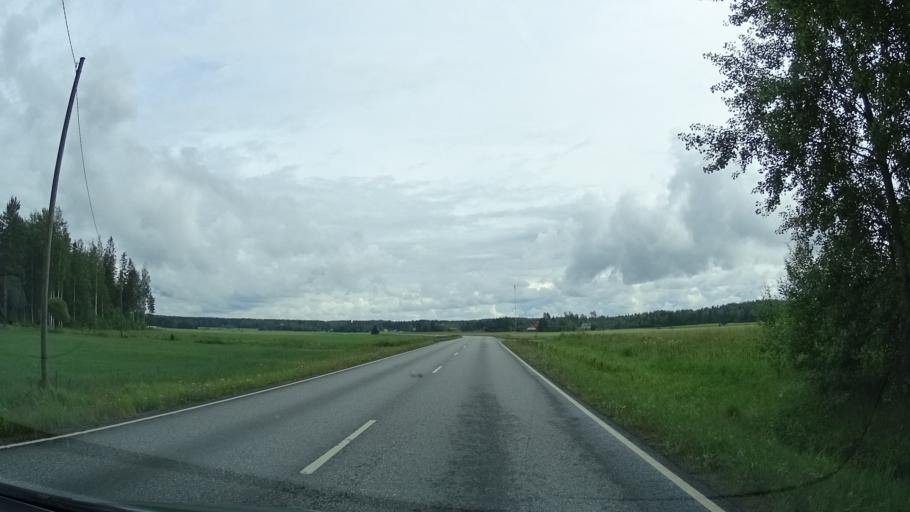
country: FI
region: Haeme
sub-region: Forssa
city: Humppila
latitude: 61.1001
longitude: 23.2939
